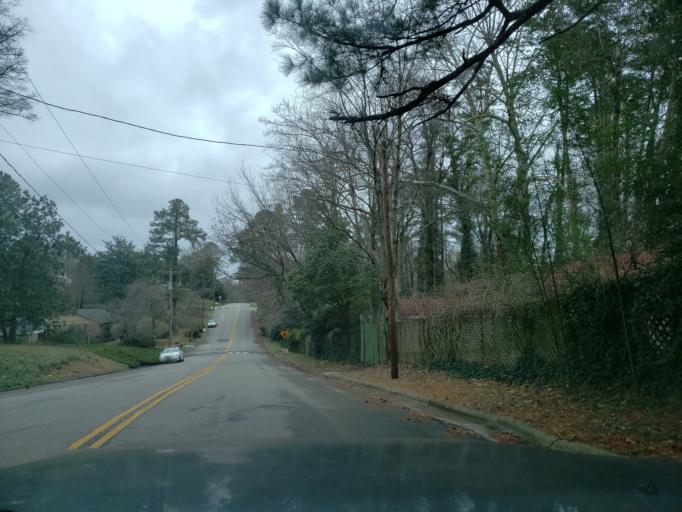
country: US
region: North Carolina
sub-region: Durham County
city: Durham
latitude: 35.9831
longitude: -78.9203
